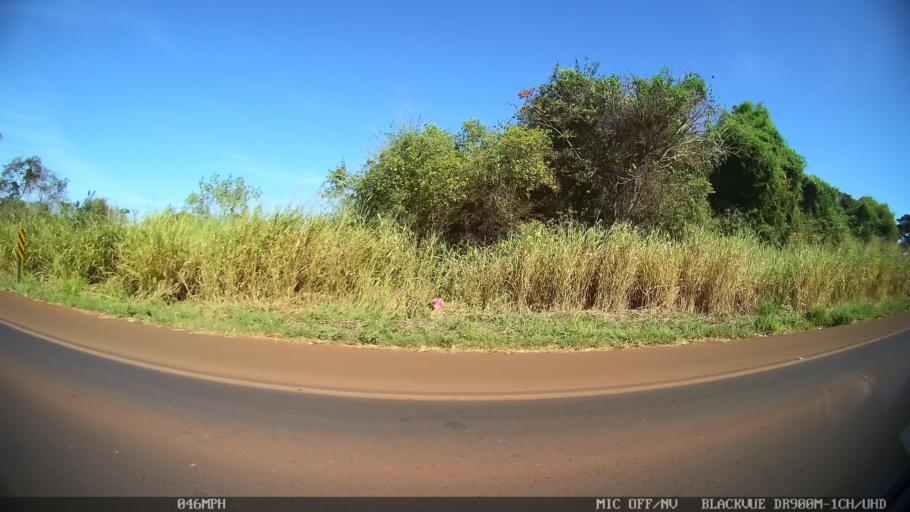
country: BR
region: Sao Paulo
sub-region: Ipua
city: Ipua
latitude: -20.5055
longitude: -47.9310
